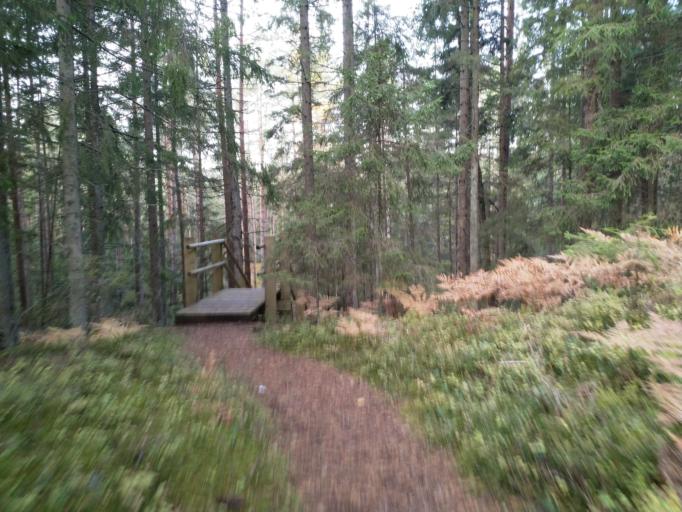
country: LV
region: Dundaga
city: Dundaga
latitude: 57.6459
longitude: 22.2607
